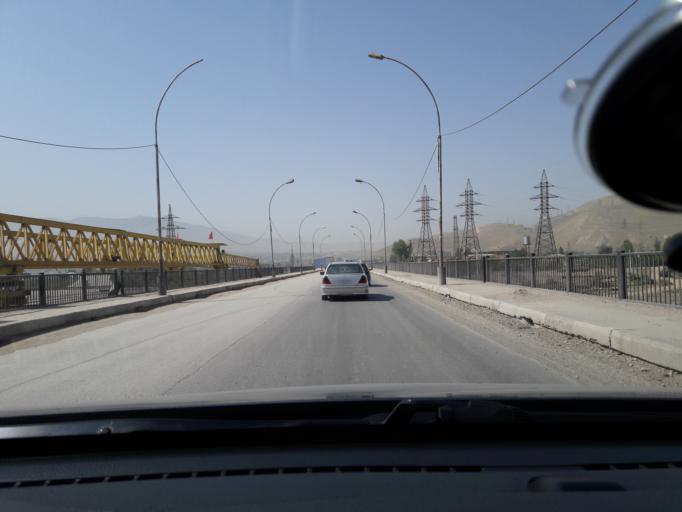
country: TJ
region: Dushanbe
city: Boshkengash
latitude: 38.4582
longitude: 68.7364
